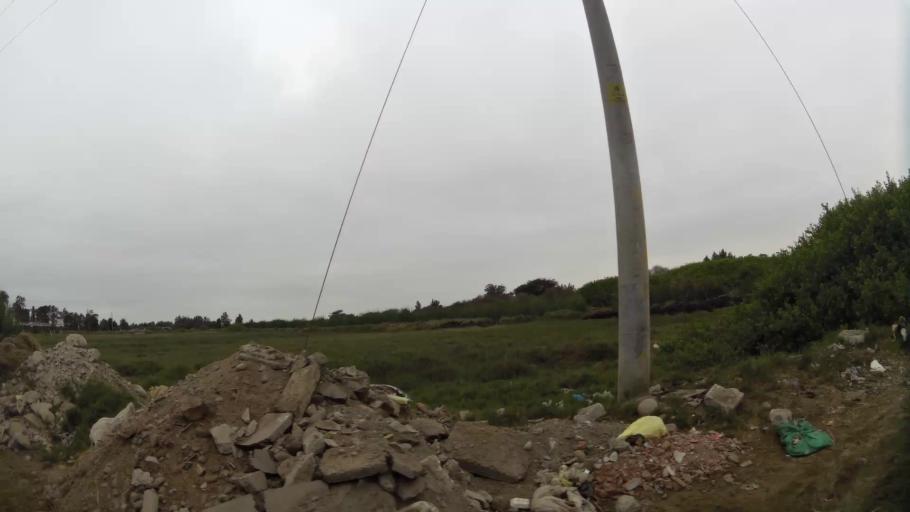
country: PE
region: Ica
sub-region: Provincia de Pisco
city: Pisco
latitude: -13.7365
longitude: -76.1977
